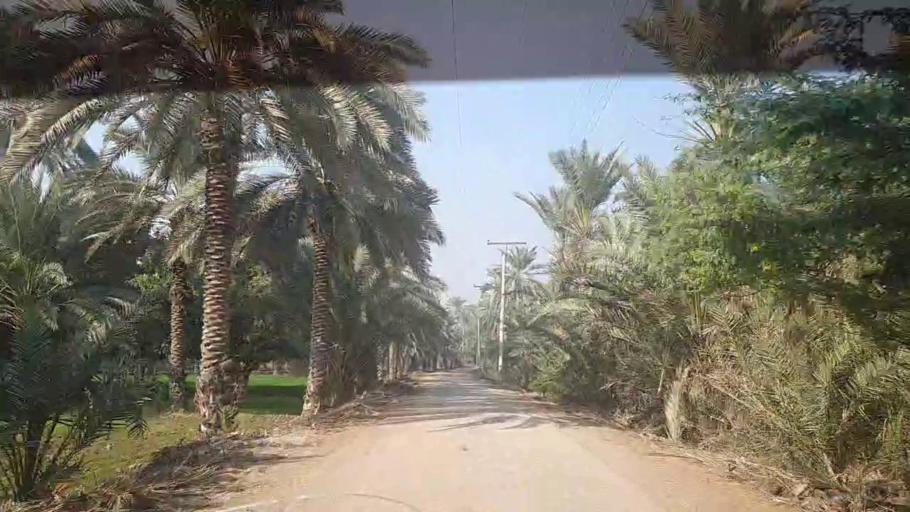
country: PK
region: Sindh
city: Khairpur
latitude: 27.4677
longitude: 68.7154
